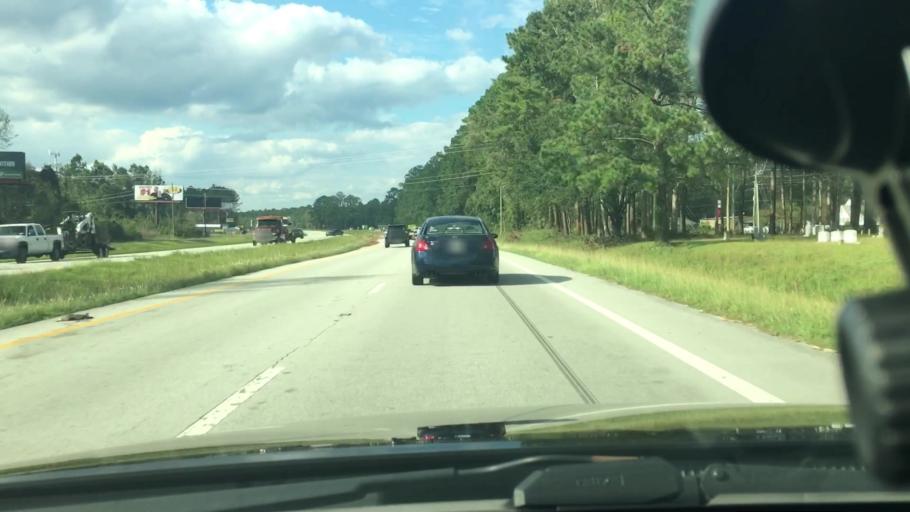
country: US
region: North Carolina
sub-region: Craven County
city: Neuse Forest
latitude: 34.9545
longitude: -76.9493
